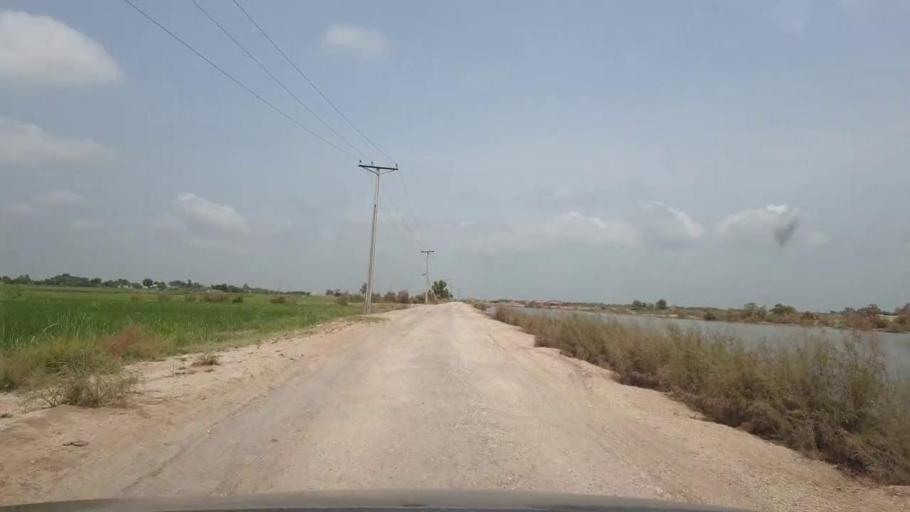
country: PK
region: Sindh
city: Ratodero
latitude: 27.9061
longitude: 68.3125
